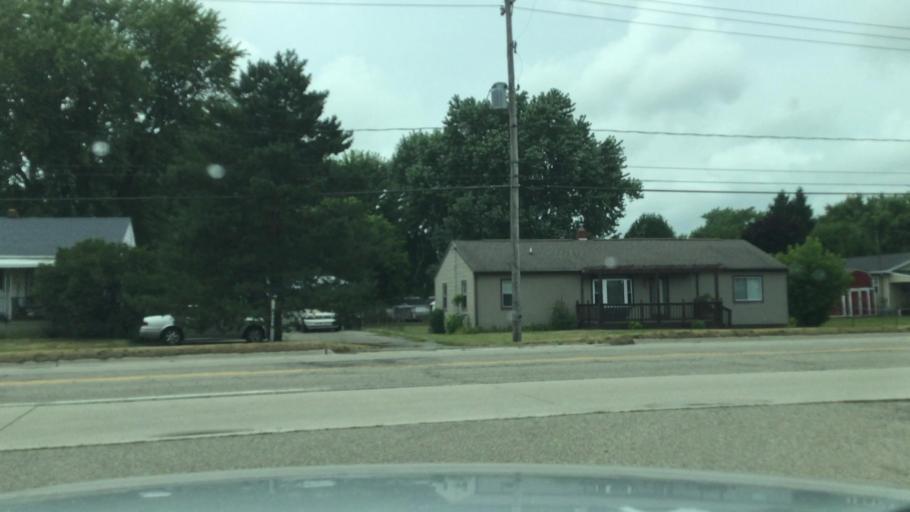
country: US
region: Michigan
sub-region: Genesee County
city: Beecher
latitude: 43.0898
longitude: -83.6168
